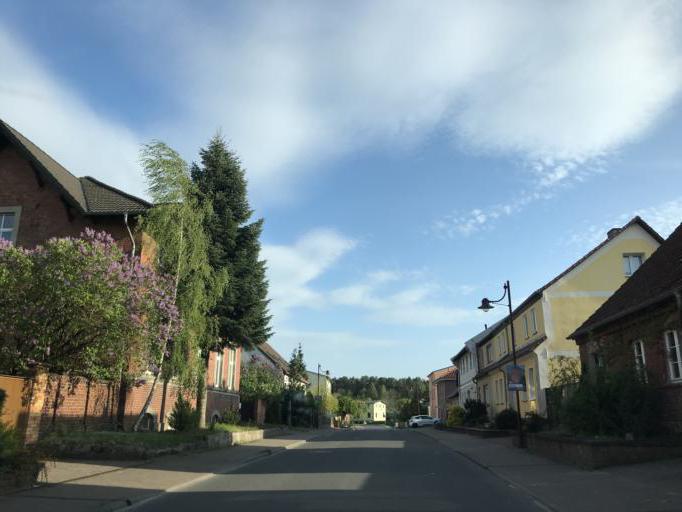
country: DE
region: Brandenburg
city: Joachimsthal
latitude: 52.9745
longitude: 13.7415
